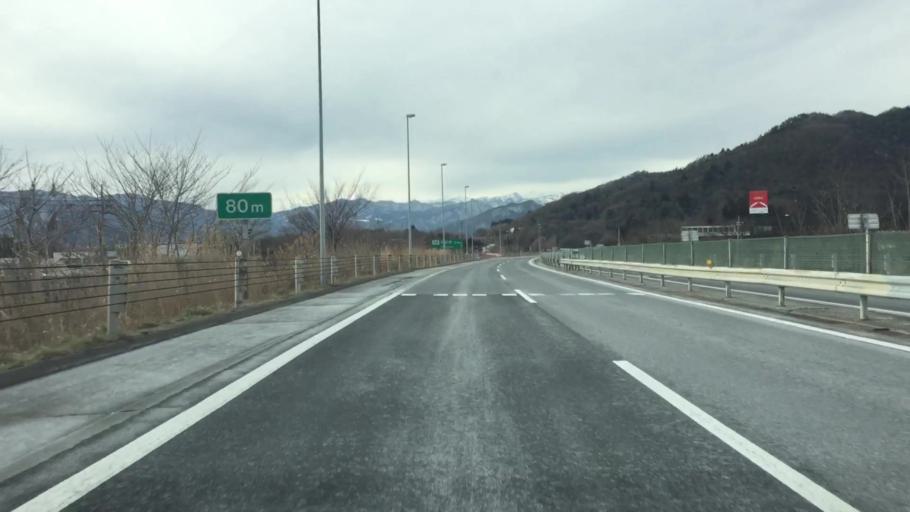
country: JP
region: Gunma
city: Numata
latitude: 36.6698
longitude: 139.0493
